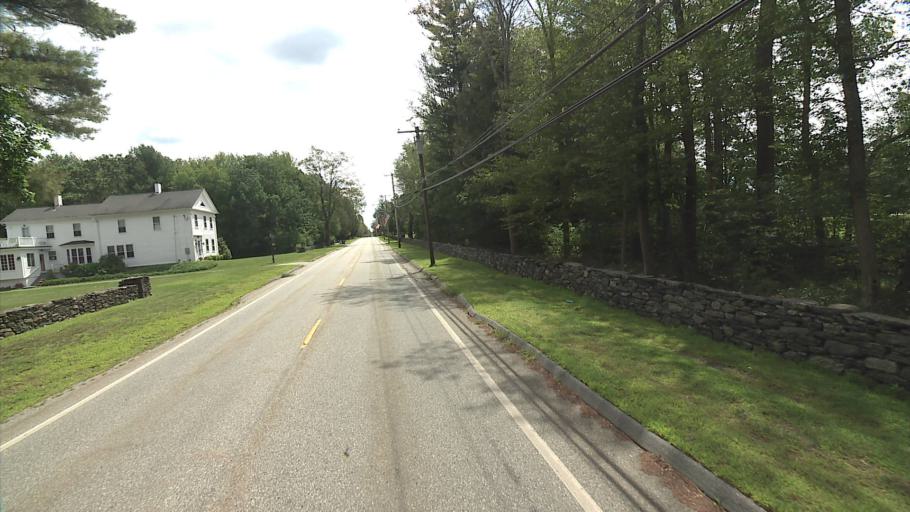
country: US
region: Connecticut
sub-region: Windham County
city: Thompson
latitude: 41.9625
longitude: -71.8679
